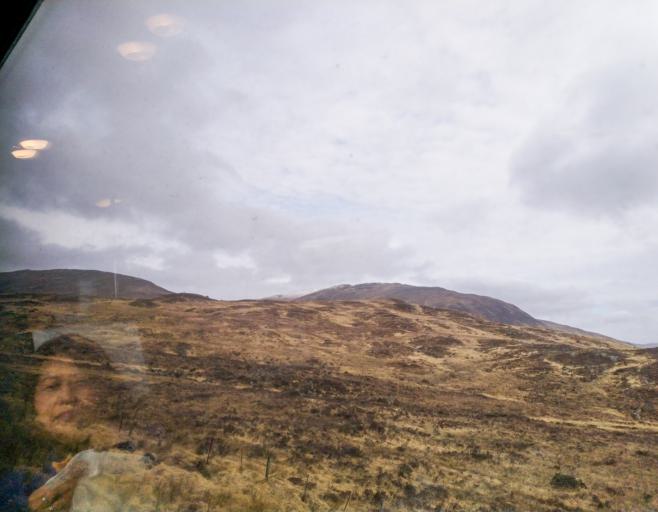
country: GB
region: Scotland
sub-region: Highland
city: Spean Bridge
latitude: 56.7003
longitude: -4.5758
